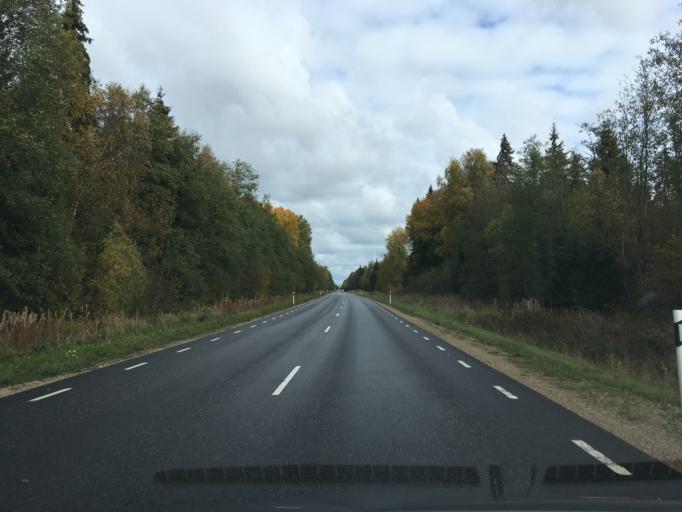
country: EE
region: Harju
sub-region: Anija vald
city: Kehra
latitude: 59.2271
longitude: 25.2751
